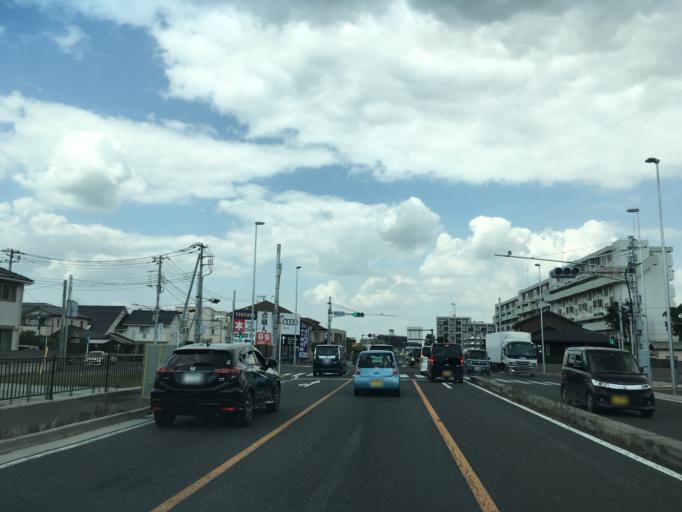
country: JP
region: Saitama
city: Sayama
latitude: 35.8452
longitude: 139.3890
